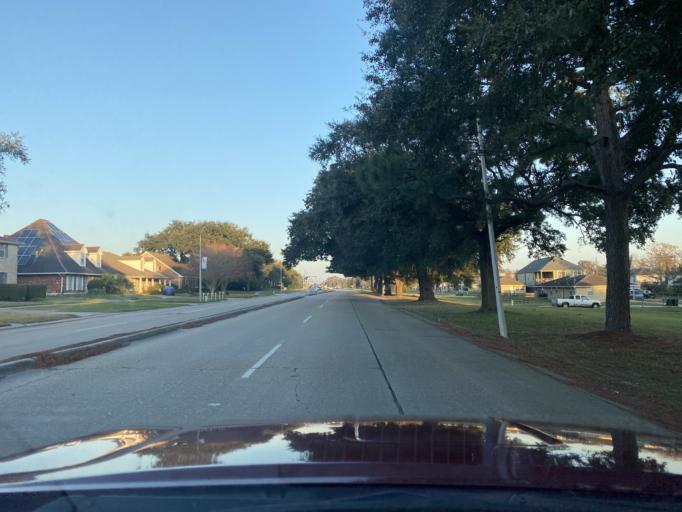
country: US
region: Louisiana
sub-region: Orleans Parish
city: New Orleans
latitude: 30.0256
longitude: -90.0563
